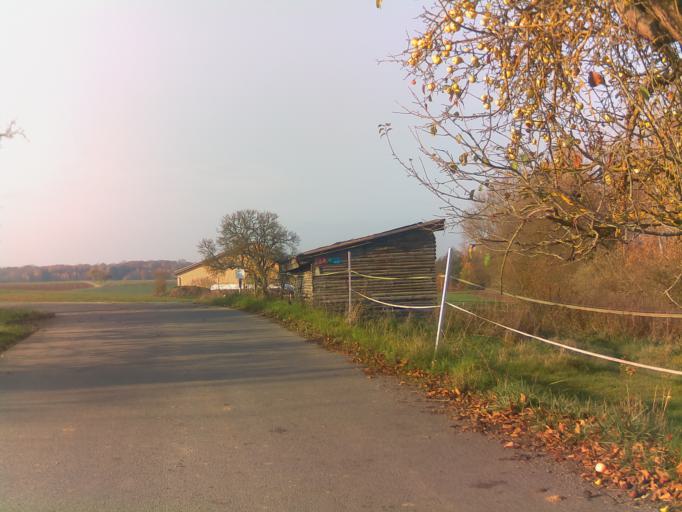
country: DE
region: Bavaria
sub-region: Regierungsbezirk Unterfranken
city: Hochheim
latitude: 50.3855
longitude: 10.4103
